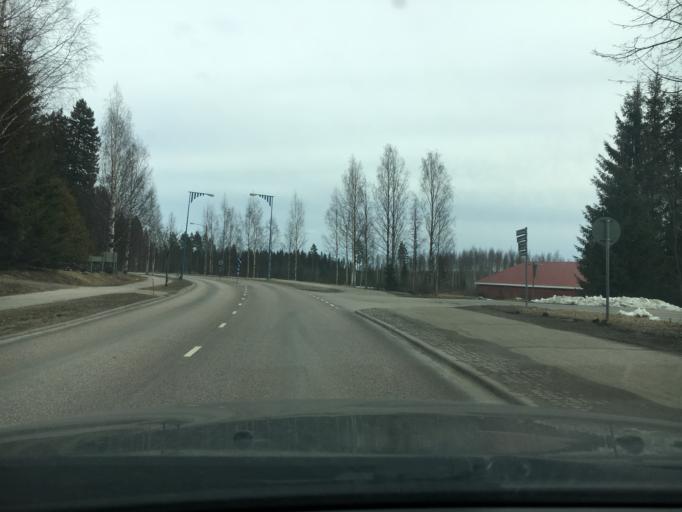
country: FI
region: Central Finland
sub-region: AEaenekoski
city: Konnevesi
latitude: 62.6269
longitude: 26.2967
